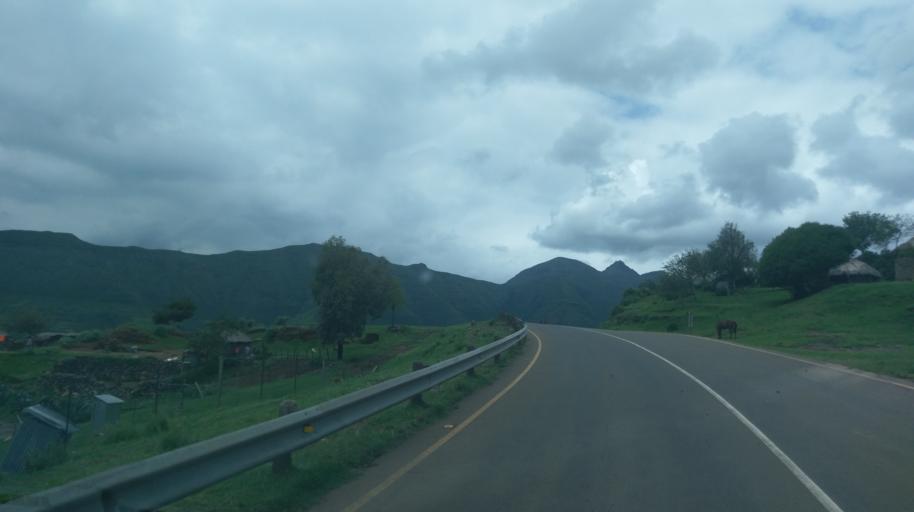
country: LS
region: Butha-Buthe
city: Butha-Buthe
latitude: -29.0362
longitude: 28.2960
